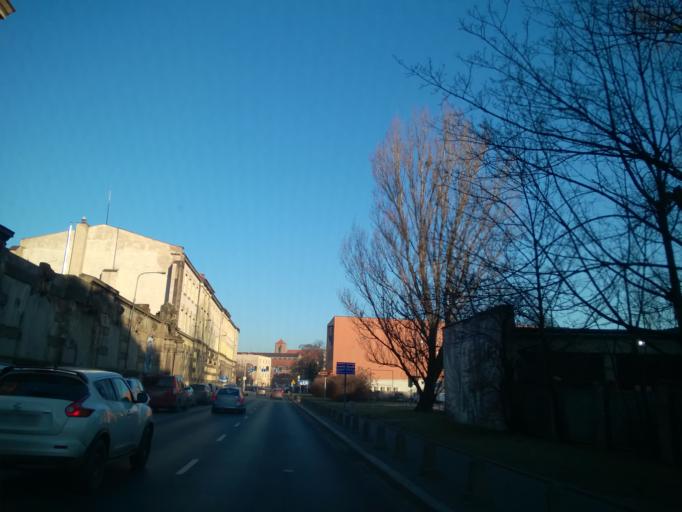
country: PL
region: Lower Silesian Voivodeship
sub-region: Powiat wroclawski
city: Wroclaw
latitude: 51.1092
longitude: 17.0408
